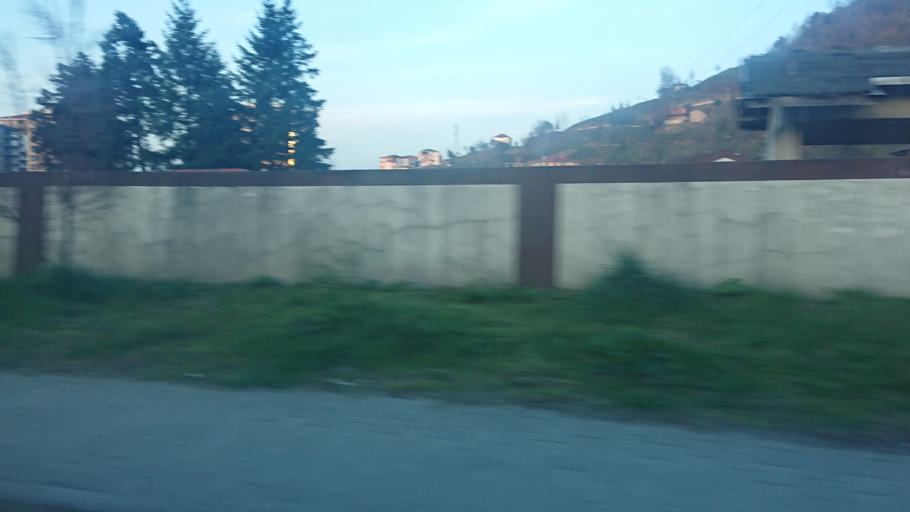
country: TR
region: Rize
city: Gundogdu
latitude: 41.0397
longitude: 40.5793
